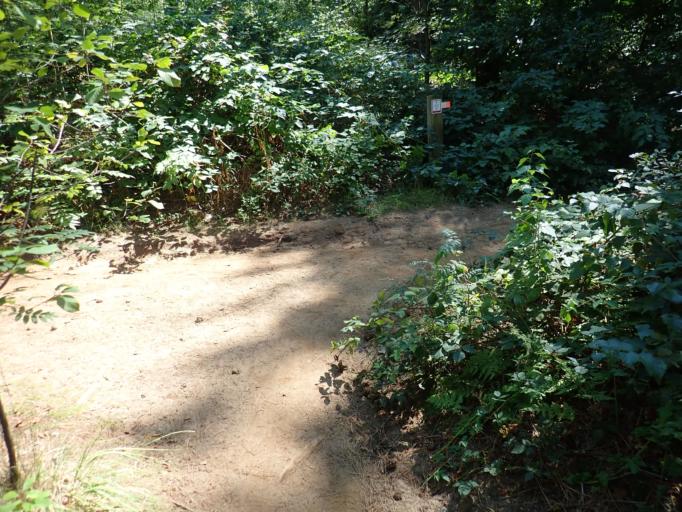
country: BE
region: Flanders
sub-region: Provincie Vlaams-Brabant
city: Scherpenheuvel-Zichem
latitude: 51.0264
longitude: 4.9653
